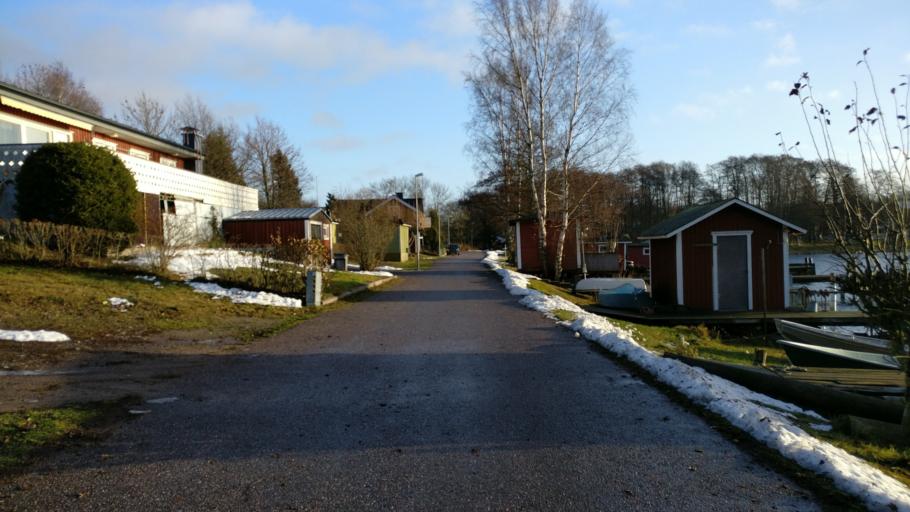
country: FI
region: Uusimaa
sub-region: Raaseporin
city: Hanko
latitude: 59.8364
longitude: 22.9300
